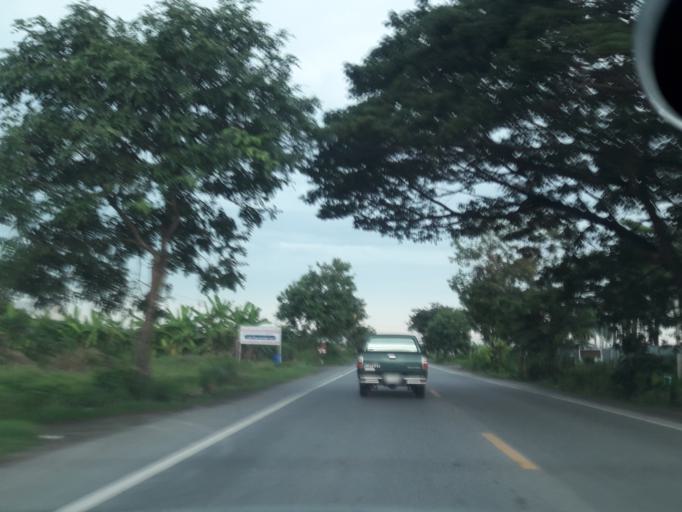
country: TH
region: Phra Nakhon Si Ayutthaya
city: Wang Noi
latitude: 14.1731
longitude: 100.7474
